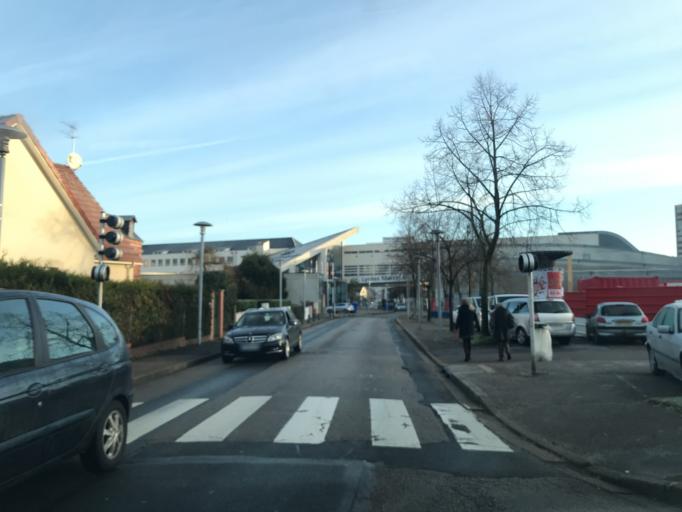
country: FR
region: Haute-Normandie
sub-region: Departement de la Seine-Maritime
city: Sotteville-les-Rouen
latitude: 49.4140
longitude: 1.0841
